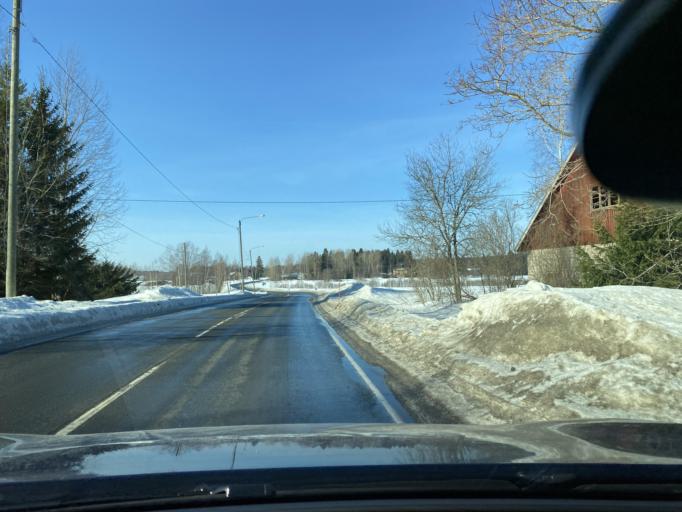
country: FI
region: Central Finland
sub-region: Joutsa
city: Joutsa
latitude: 61.8108
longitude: 25.9556
